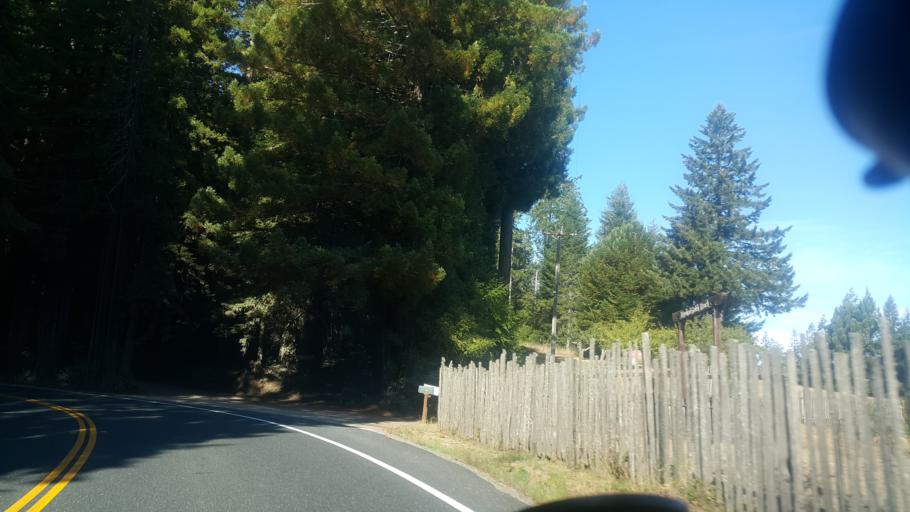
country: US
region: California
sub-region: Mendocino County
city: Fort Bragg
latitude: 39.4076
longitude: -123.7281
